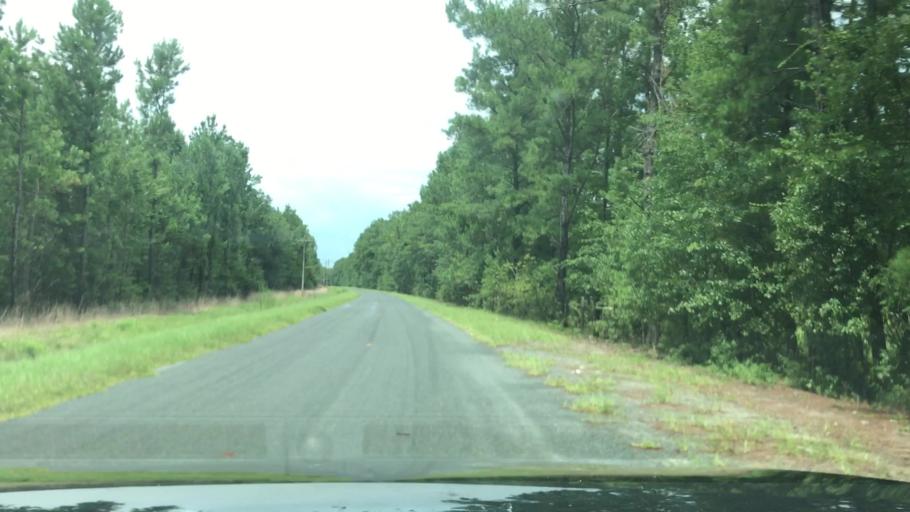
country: US
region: South Carolina
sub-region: Colleton County
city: Walterboro
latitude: 33.0066
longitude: -80.6693
